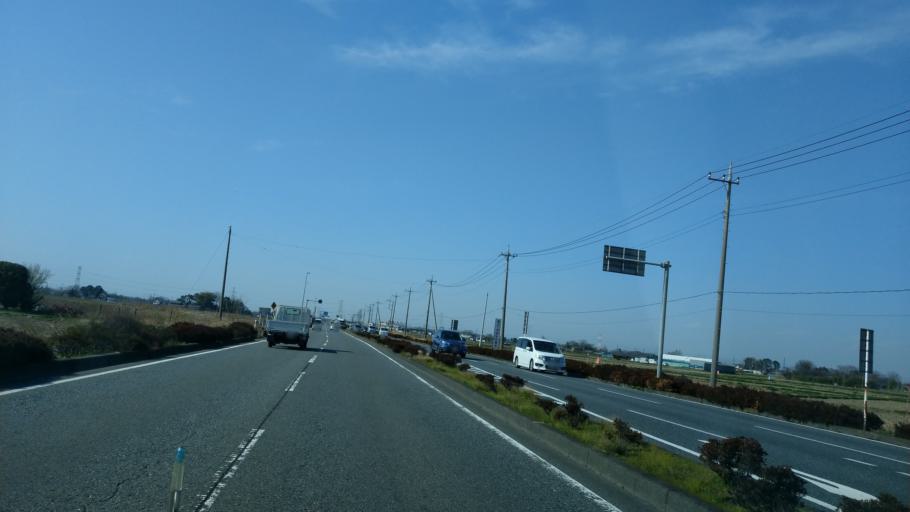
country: JP
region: Saitama
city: Sakado
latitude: 35.9889
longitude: 139.4593
